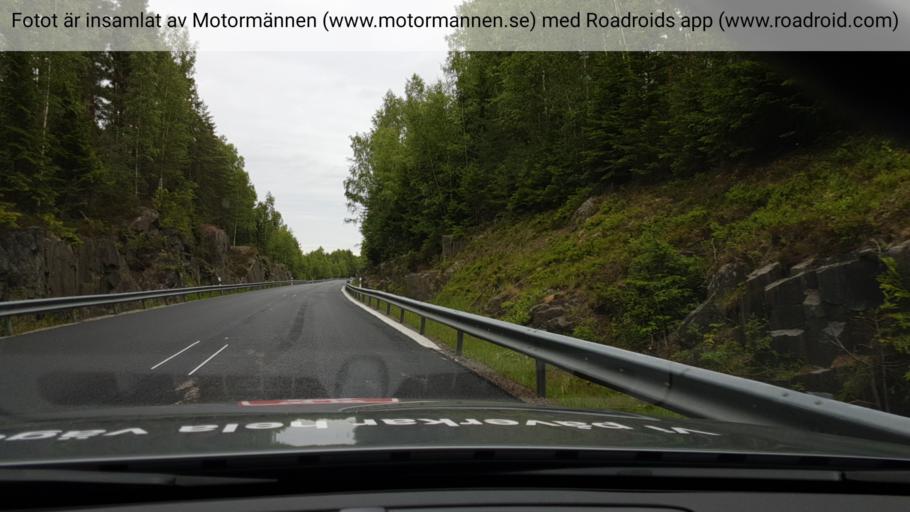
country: SE
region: Vaestmanland
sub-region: Skinnskattebergs Kommun
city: Skinnskatteberg
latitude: 59.8574
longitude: 15.5893
